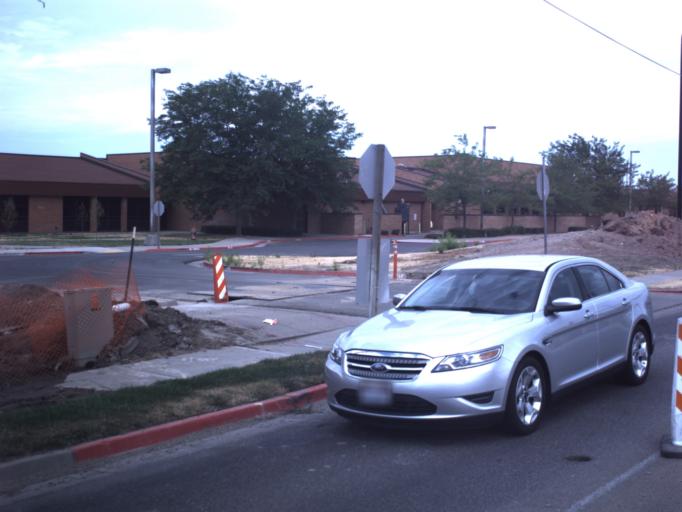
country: US
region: Utah
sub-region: Davis County
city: Syracuse
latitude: 41.0917
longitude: -112.0647
